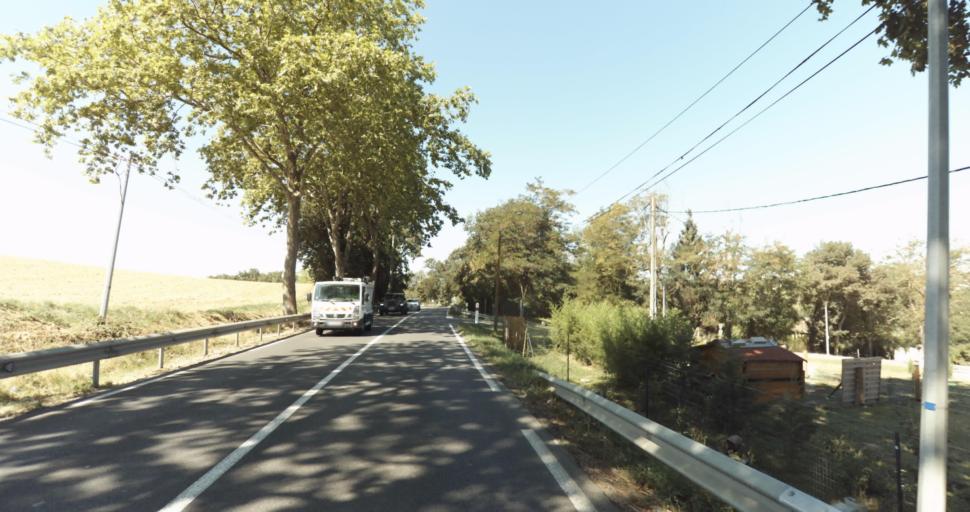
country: FR
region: Midi-Pyrenees
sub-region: Departement de la Haute-Garonne
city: Montrabe
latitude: 43.6446
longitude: 1.5096
